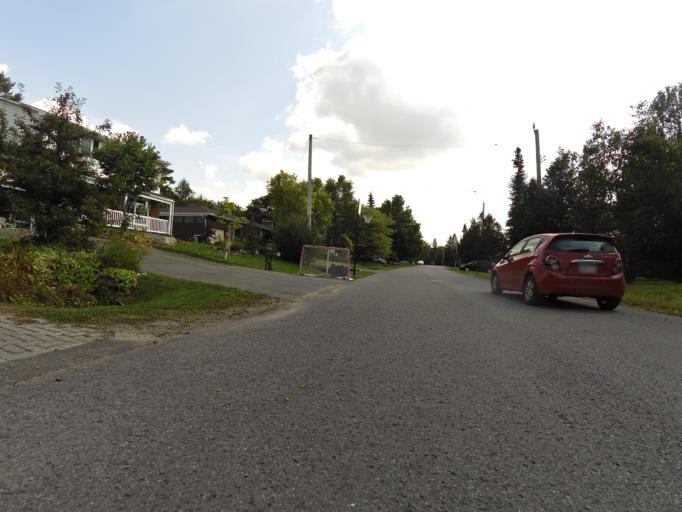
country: CA
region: Ontario
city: Bells Corners
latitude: 45.2373
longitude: -75.6998
